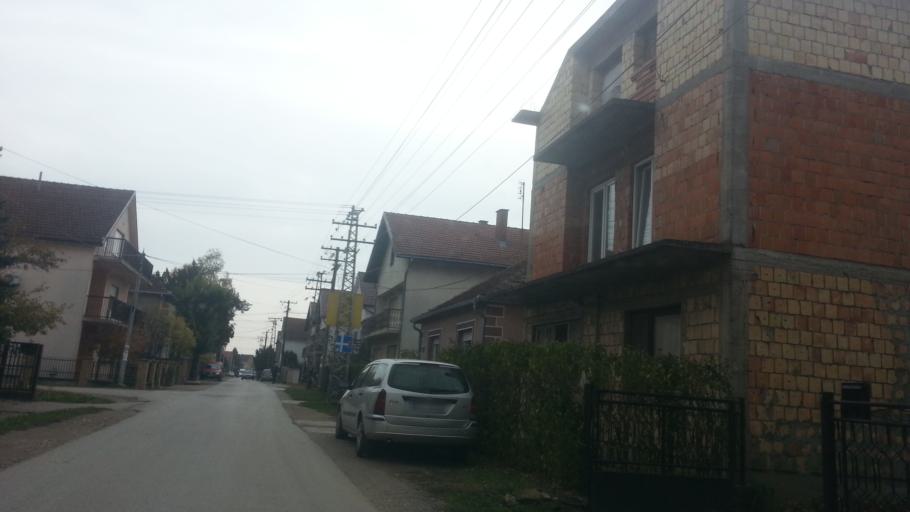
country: RS
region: Autonomna Pokrajina Vojvodina
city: Nova Pazova
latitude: 44.9530
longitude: 20.2127
